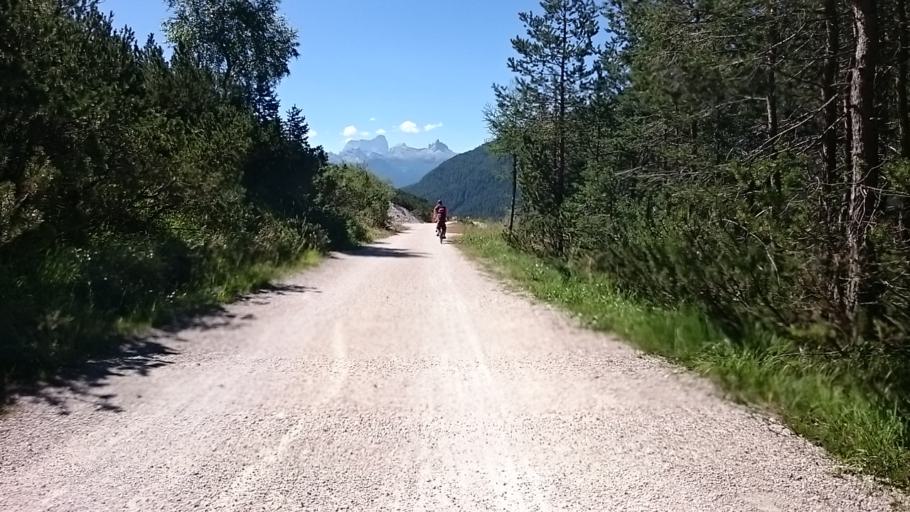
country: IT
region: Veneto
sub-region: Provincia di Belluno
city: Cortina d'Ampezzo
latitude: 46.5868
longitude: 12.1156
